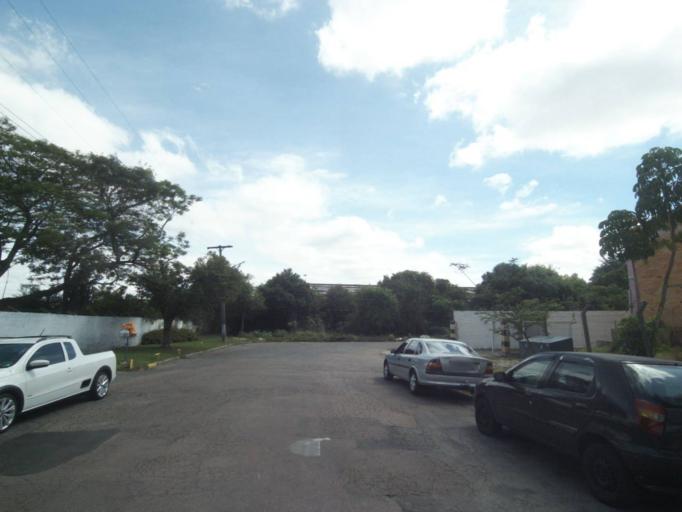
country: BR
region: Parana
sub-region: Curitiba
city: Curitiba
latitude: -25.4919
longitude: -49.3312
